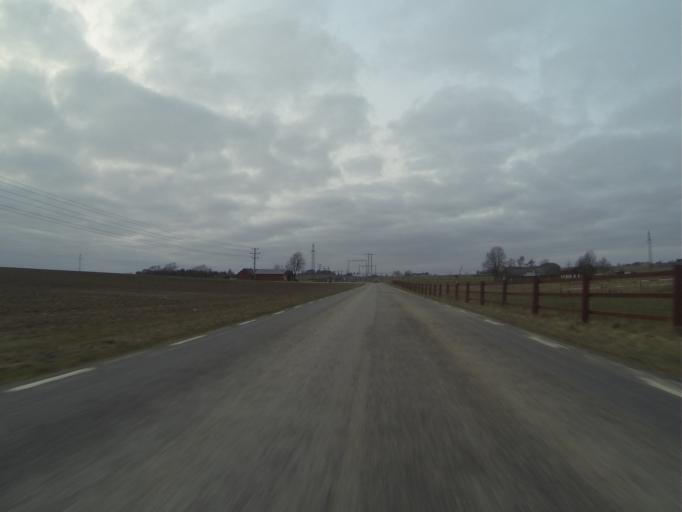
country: SE
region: Skane
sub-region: Lunds Kommun
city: Genarp
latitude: 55.6335
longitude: 13.3741
